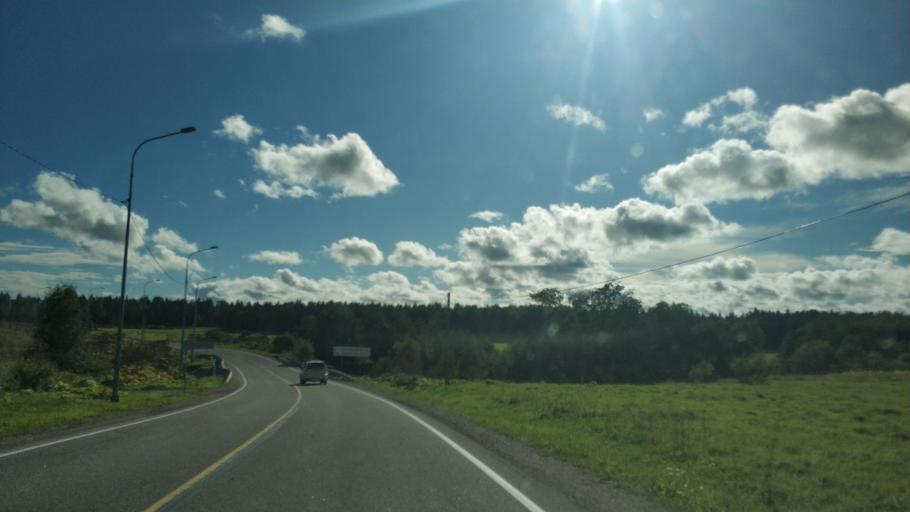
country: RU
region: Republic of Karelia
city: Khelyulya
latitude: 61.6465
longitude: 30.5839
